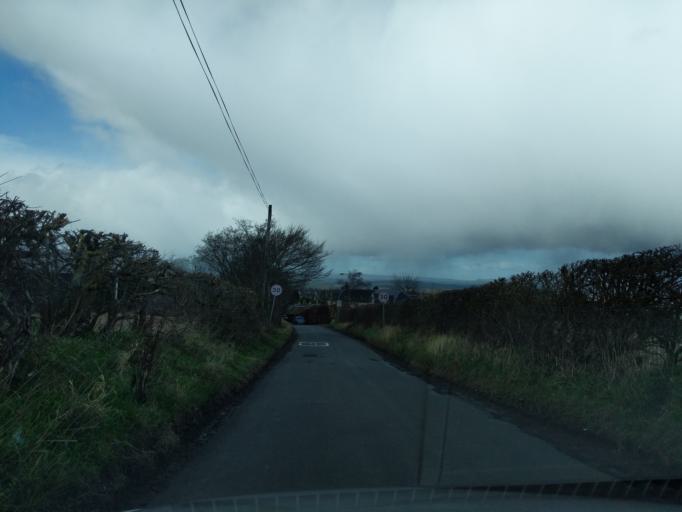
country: GB
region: Scotland
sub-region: Edinburgh
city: Currie
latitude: 55.8924
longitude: -3.3059
